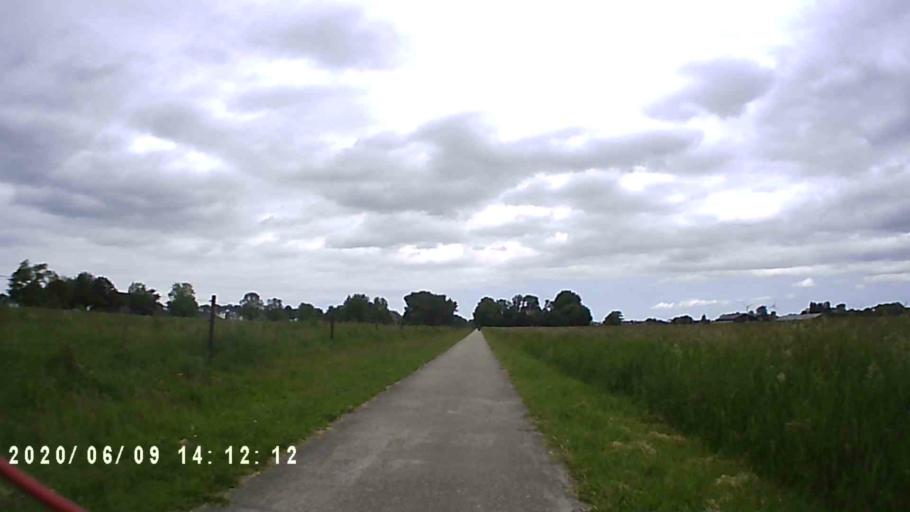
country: NL
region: Groningen
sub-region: Gemeente Bedum
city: Bedum
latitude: 53.2732
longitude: 6.6040
